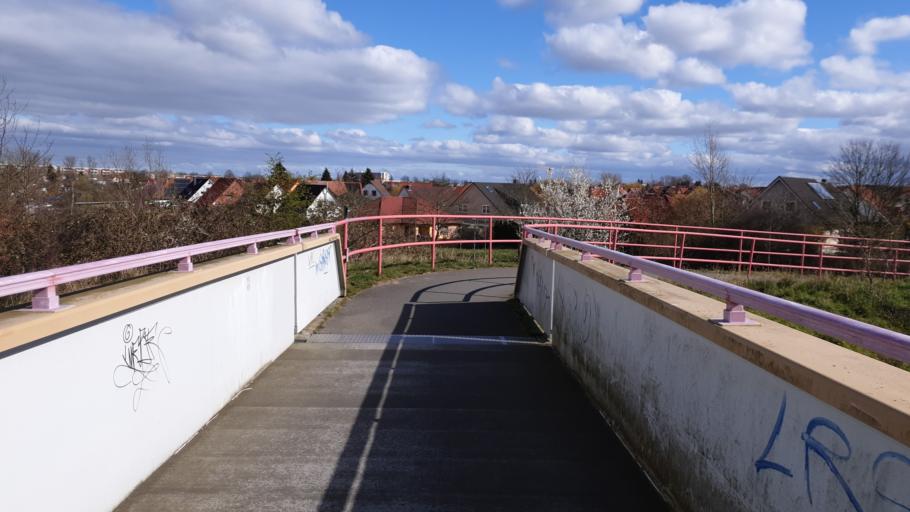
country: DE
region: Mecklenburg-Vorpommern
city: Lankow
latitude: 53.6400
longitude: 11.3515
